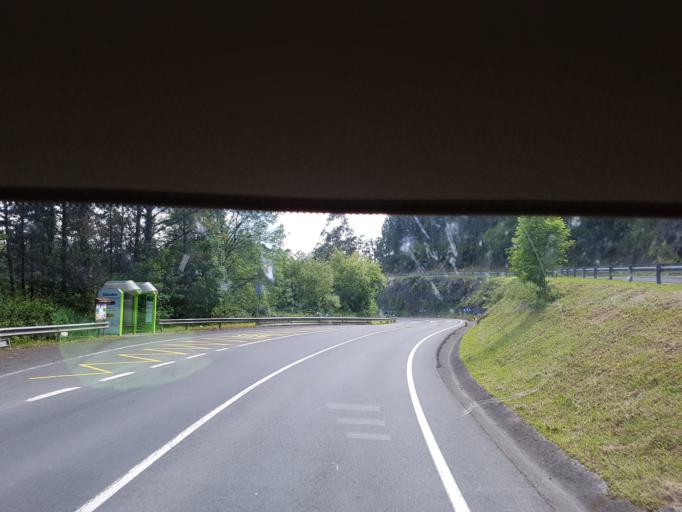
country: ES
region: Basque Country
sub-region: Bizkaia
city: Sopuerta
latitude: 43.2909
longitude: -3.1298
